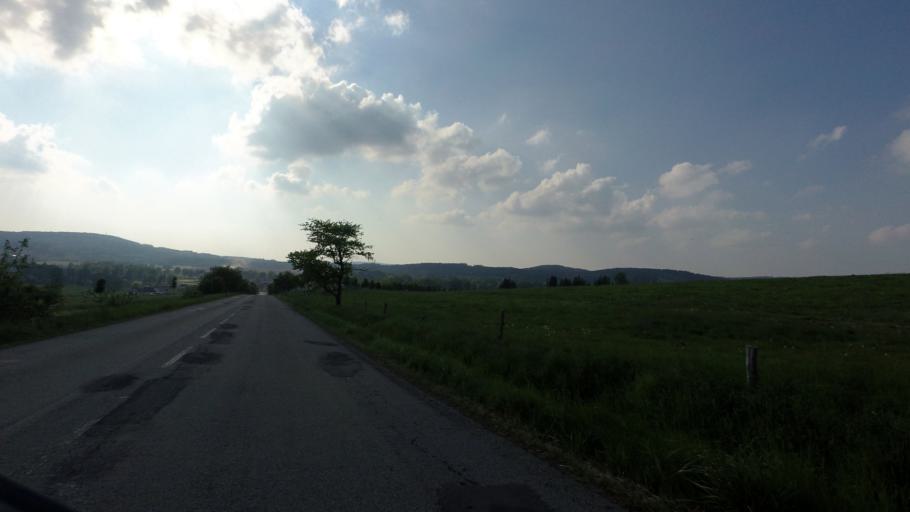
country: CZ
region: Ustecky
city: Velky Senov
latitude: 51.0093
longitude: 14.3698
